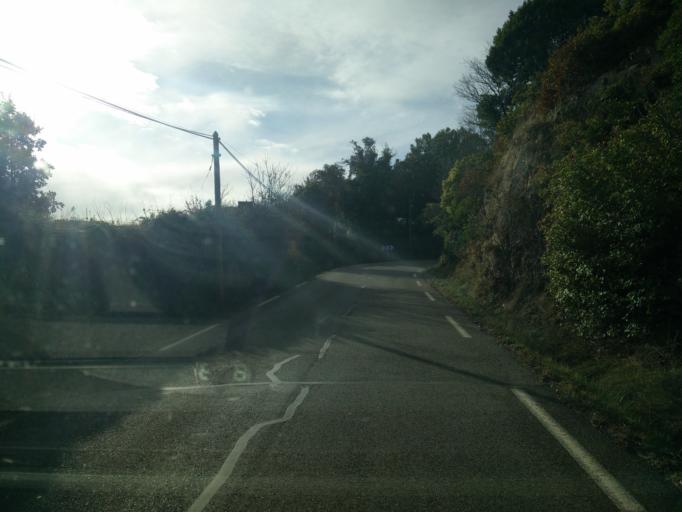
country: FR
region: Provence-Alpes-Cote d'Azur
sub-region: Departement du Var
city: Cotignac
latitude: 43.5337
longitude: 6.1423
